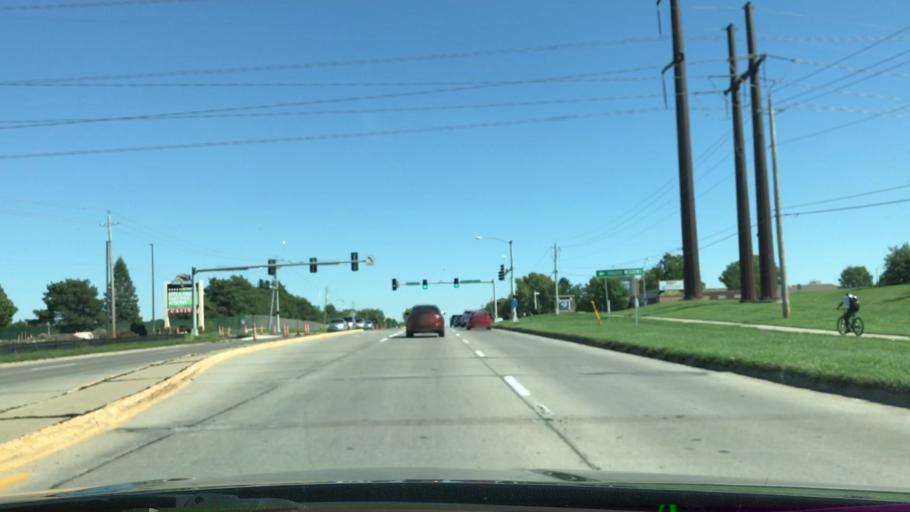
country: US
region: Iowa
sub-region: Polk County
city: Altoona
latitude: 41.6441
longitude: -93.4993
